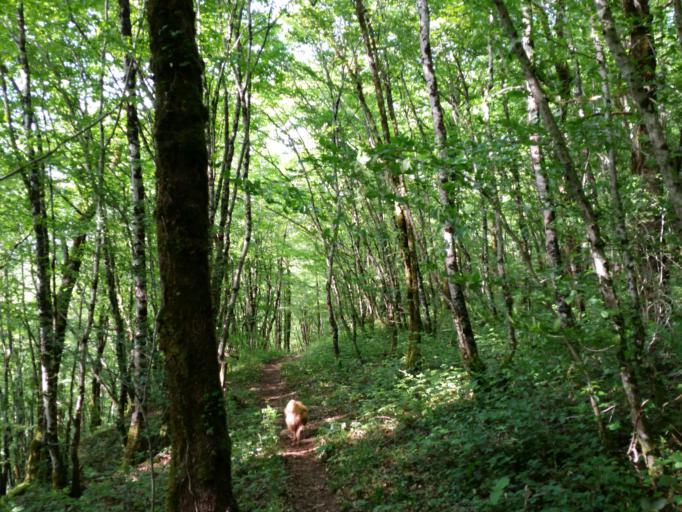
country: FR
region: Franche-Comte
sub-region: Departement du Doubs
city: Quingey
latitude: 47.0529
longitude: 5.9843
